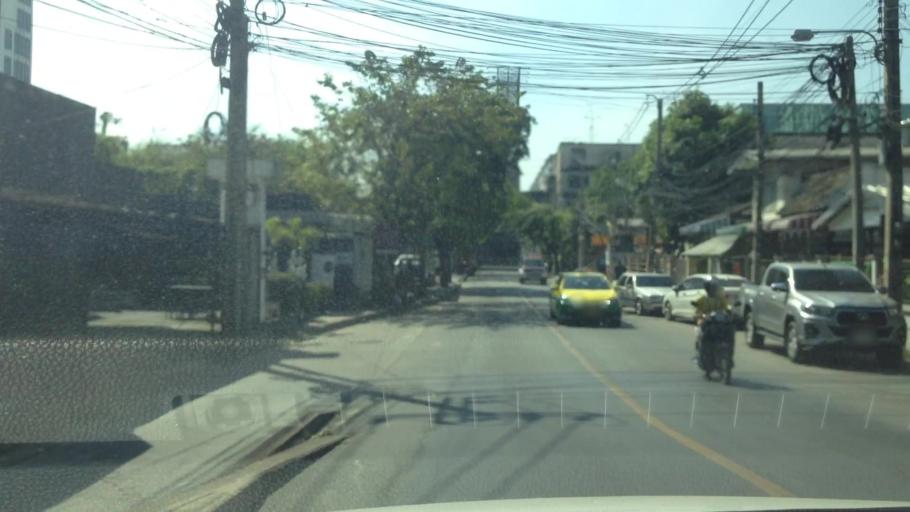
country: TH
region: Bangkok
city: Bang Kapi
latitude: 13.7627
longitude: 100.6339
